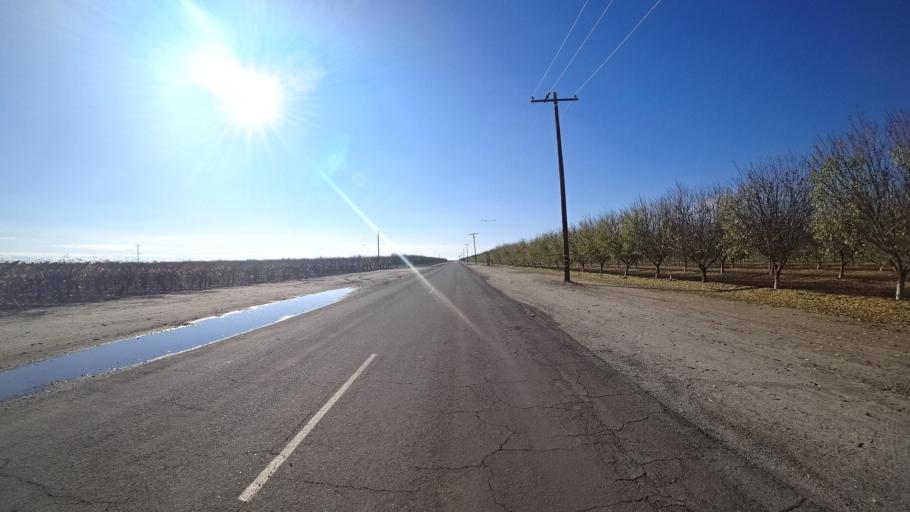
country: US
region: California
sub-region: Kern County
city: Delano
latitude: 35.7407
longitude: -119.2763
